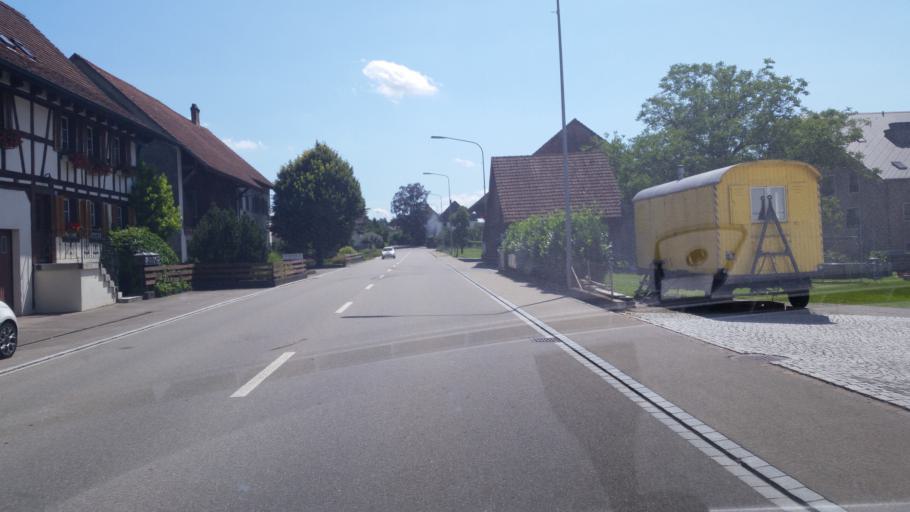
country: CH
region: Zurich
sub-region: Bezirk Buelach
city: Glattfelden
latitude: 47.5583
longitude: 8.5035
